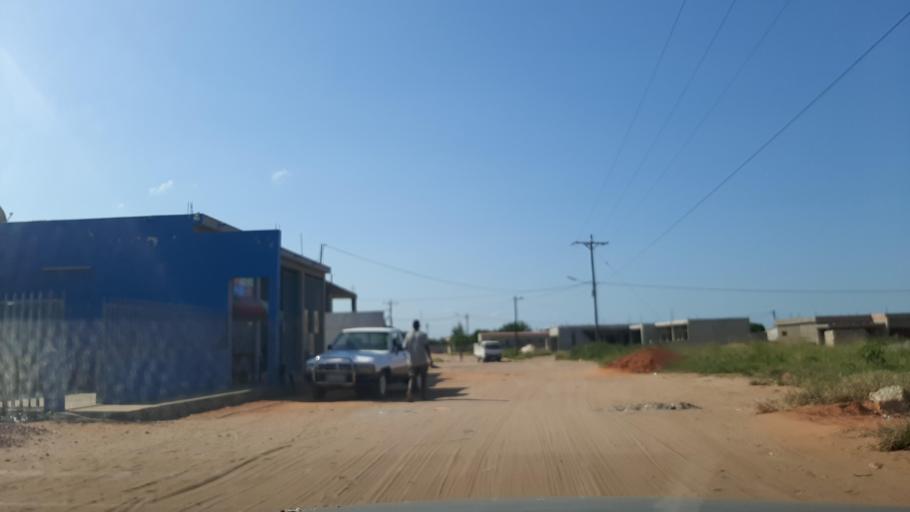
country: MZ
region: Maputo
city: Matola
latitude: -25.8003
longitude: 32.4909
